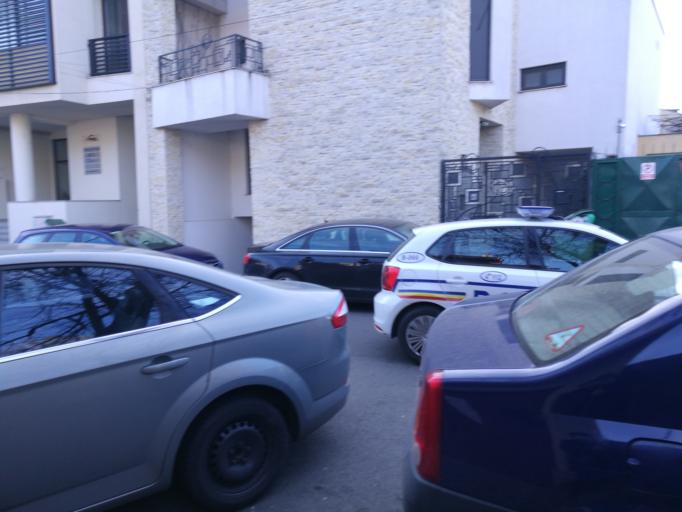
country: RO
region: Bucuresti
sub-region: Municipiul Bucuresti
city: Bucharest
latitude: 44.4353
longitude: 26.1314
